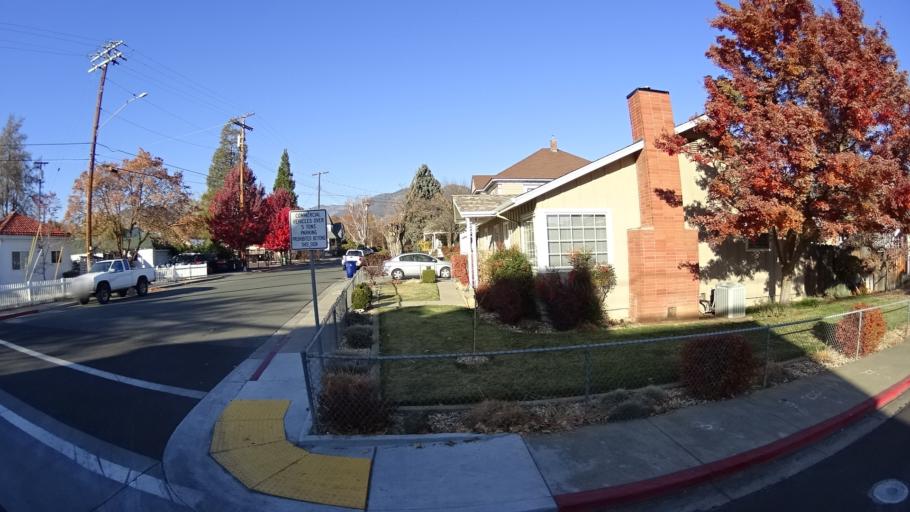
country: US
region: California
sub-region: Siskiyou County
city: Yreka
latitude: 41.7331
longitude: -122.6380
